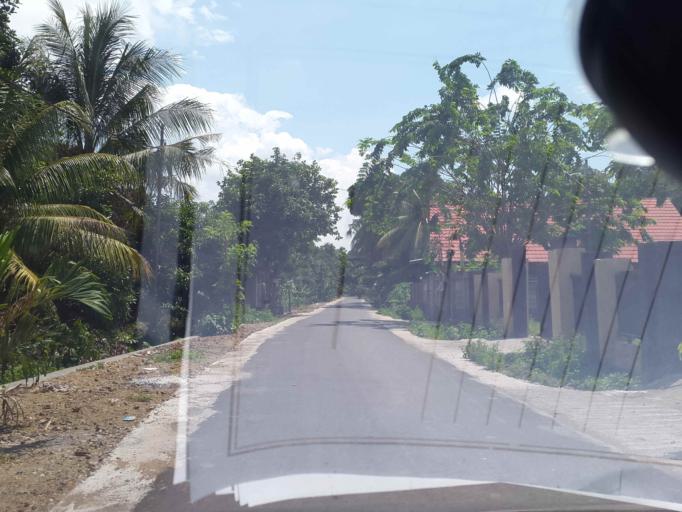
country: ID
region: West Nusa Tenggara
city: Jelateng Timur
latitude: -8.7145
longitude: 116.0755
